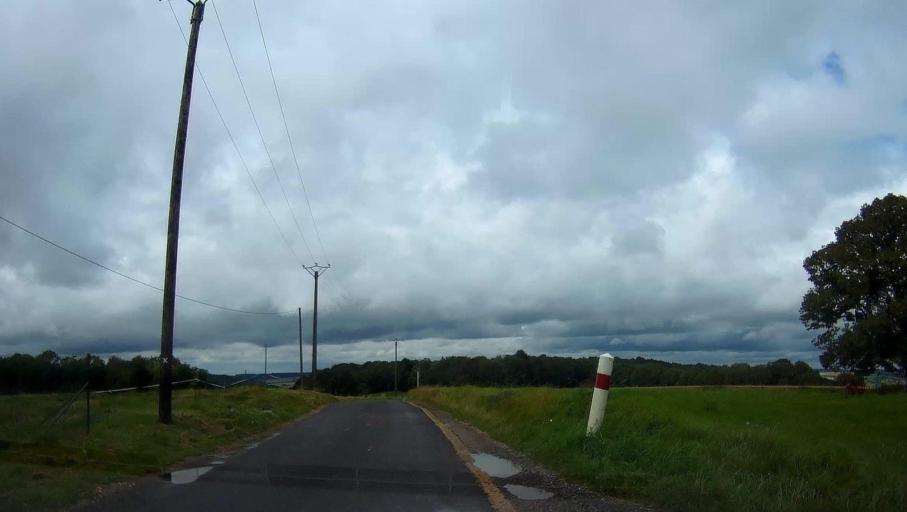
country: FR
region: Champagne-Ardenne
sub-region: Departement des Ardennes
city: Rimogne
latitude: 49.7636
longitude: 4.5040
